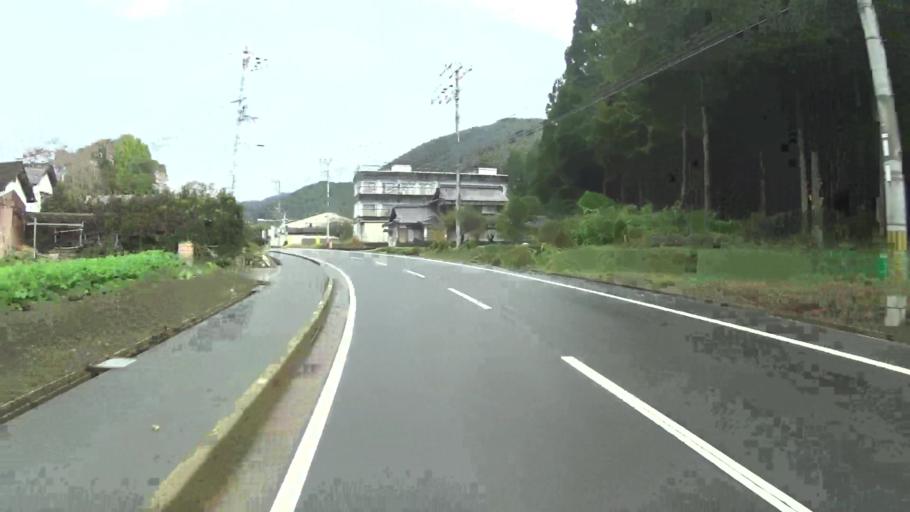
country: JP
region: Kyoto
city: Fukuchiyama
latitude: 35.4017
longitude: 135.1488
